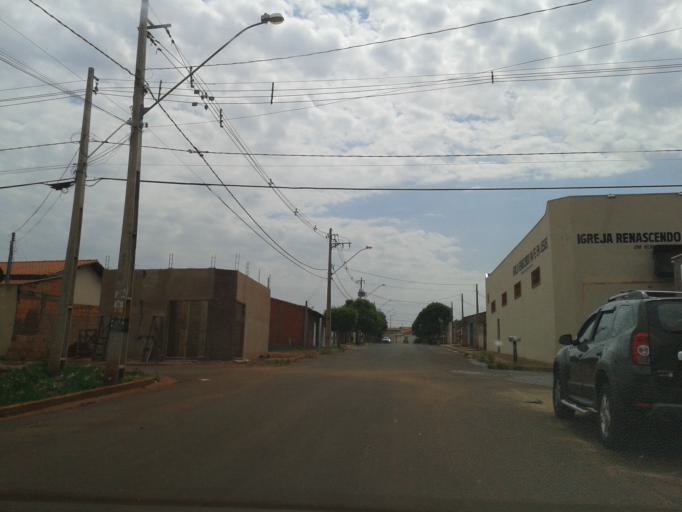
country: BR
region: Minas Gerais
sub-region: Ituiutaba
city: Ituiutaba
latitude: -18.9839
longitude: -49.4373
